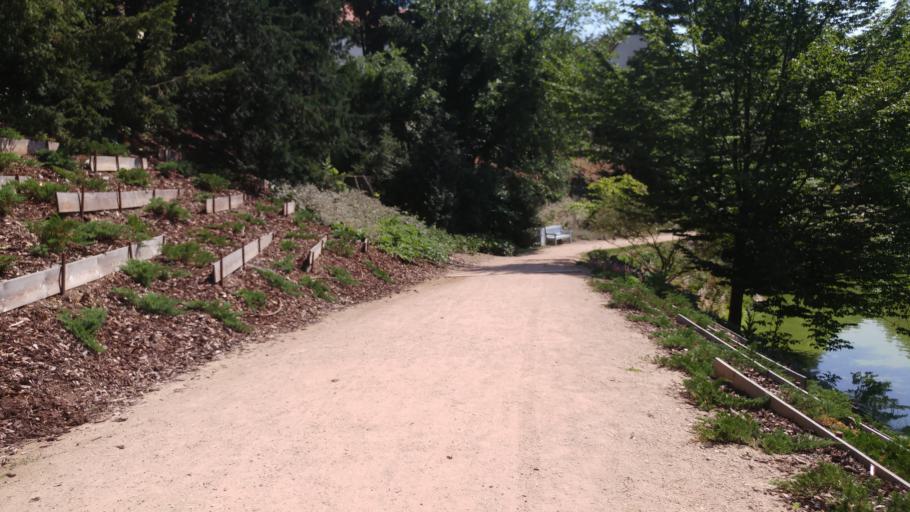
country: CZ
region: Central Bohemia
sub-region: Okres Praha-Zapad
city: Pruhonice
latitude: 50.0002
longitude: 14.5576
